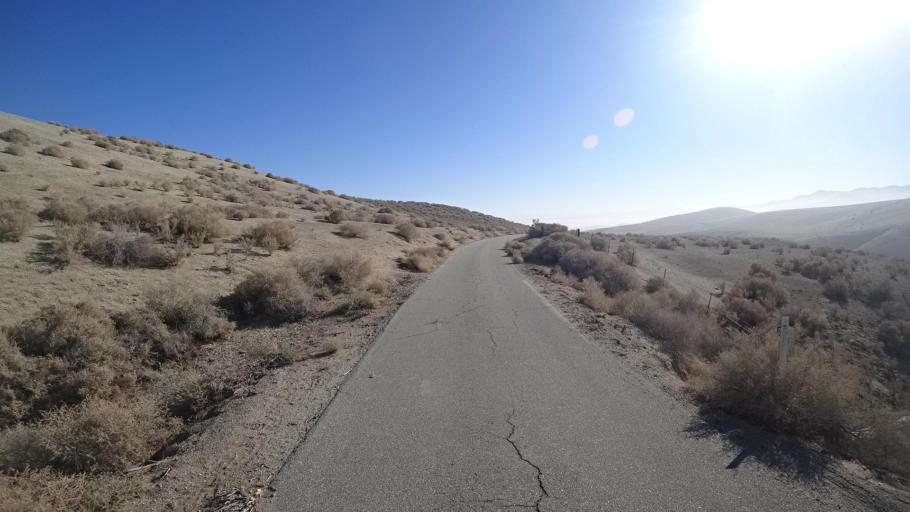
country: US
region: California
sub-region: Kern County
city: Taft Heights
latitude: 35.2336
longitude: -119.6560
